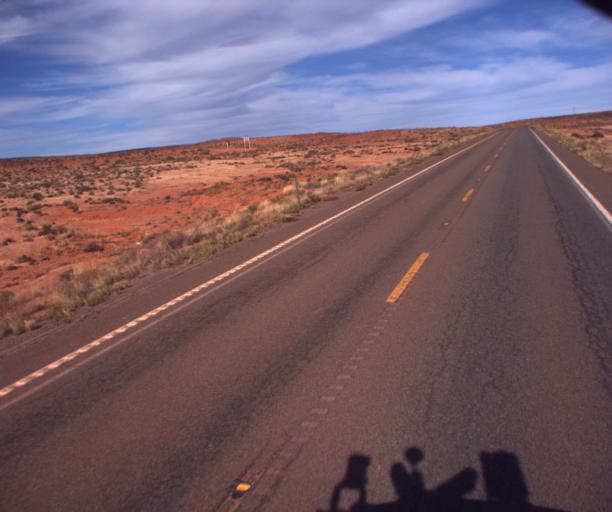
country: US
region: Arizona
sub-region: Navajo County
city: Kayenta
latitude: 36.8931
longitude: -109.8002
